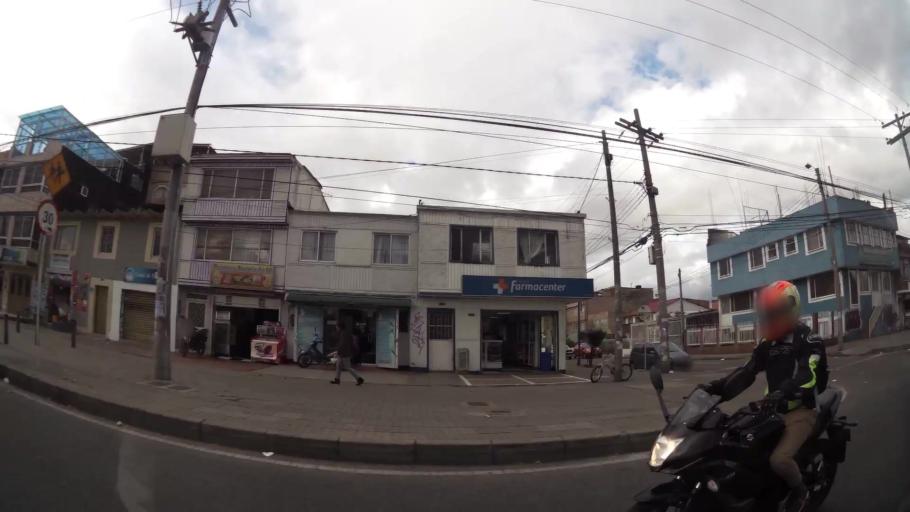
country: CO
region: Bogota D.C.
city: Barrio San Luis
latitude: 4.7126
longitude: -74.0971
